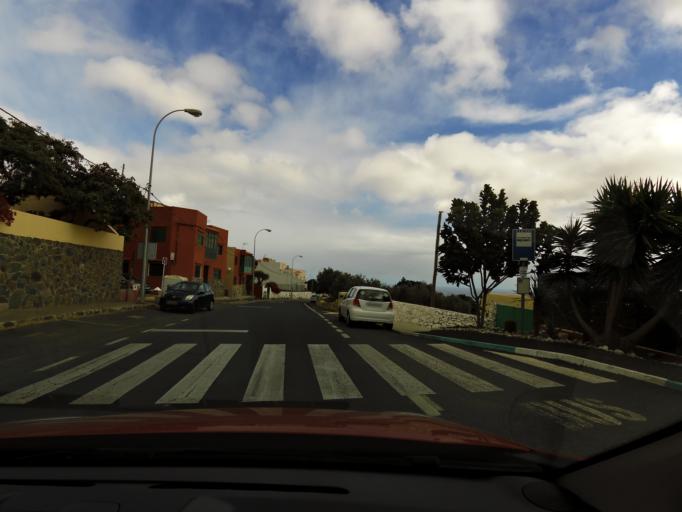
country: ES
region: Canary Islands
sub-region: Provincia de Las Palmas
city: Ingenio
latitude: 27.9258
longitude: -15.4339
